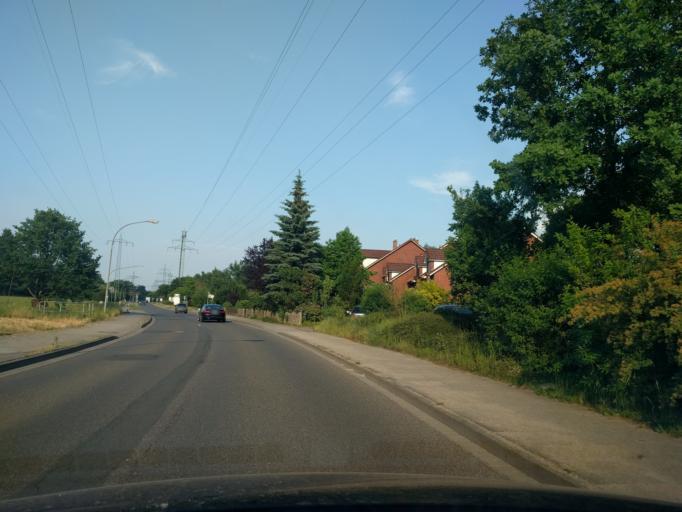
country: DE
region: Lower Saxony
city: Seevetal
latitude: 53.3871
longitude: 9.9762
